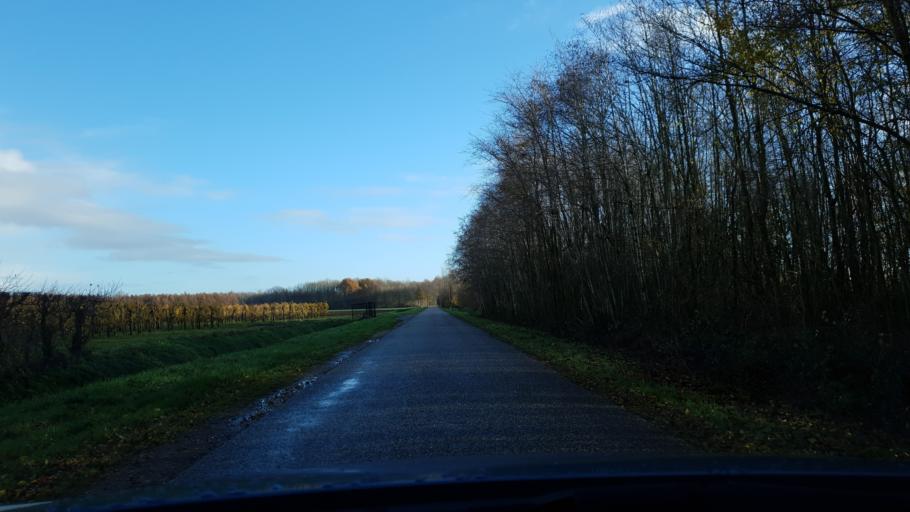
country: NL
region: Gelderland
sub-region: Gemeente Wijchen
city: Bergharen
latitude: 51.8408
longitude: 5.6577
